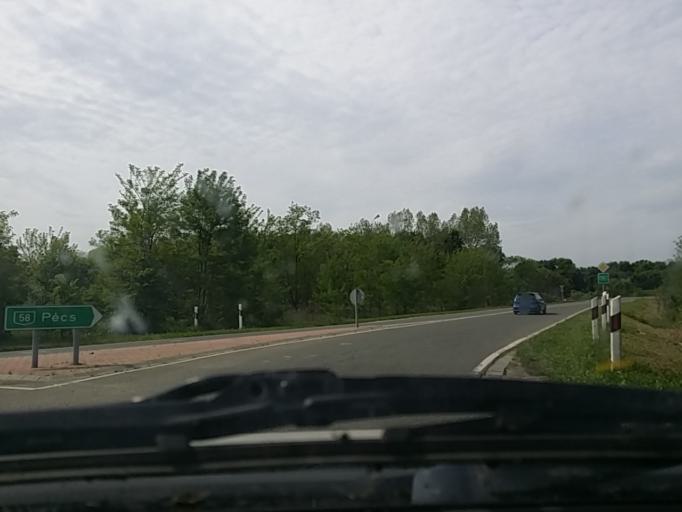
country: HU
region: Baranya
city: Harkany
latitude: 45.8447
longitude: 18.2219
